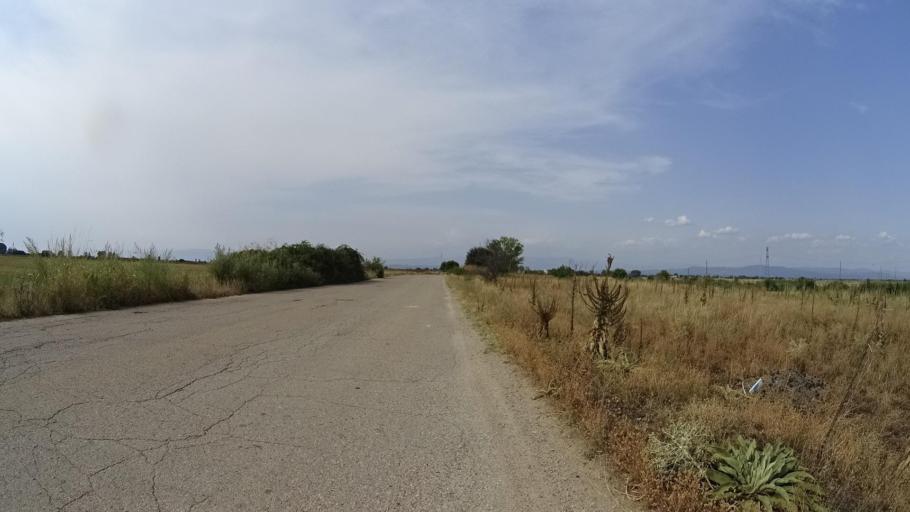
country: BG
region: Plovdiv
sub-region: Obshtina Kaloyanovo
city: Kaloyanovo
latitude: 42.3174
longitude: 24.7992
